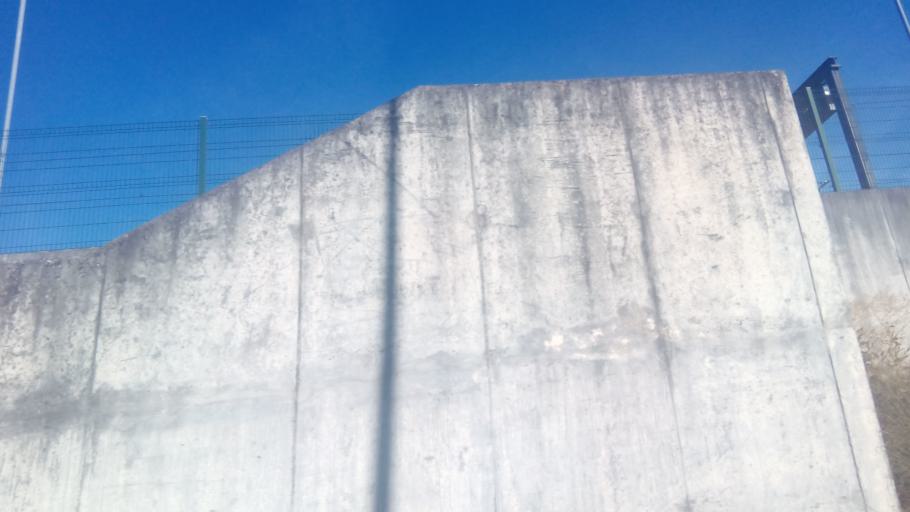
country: PT
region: Porto
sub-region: Paredes
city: Casteloes de Cepeda
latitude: 41.1930
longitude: -8.3378
